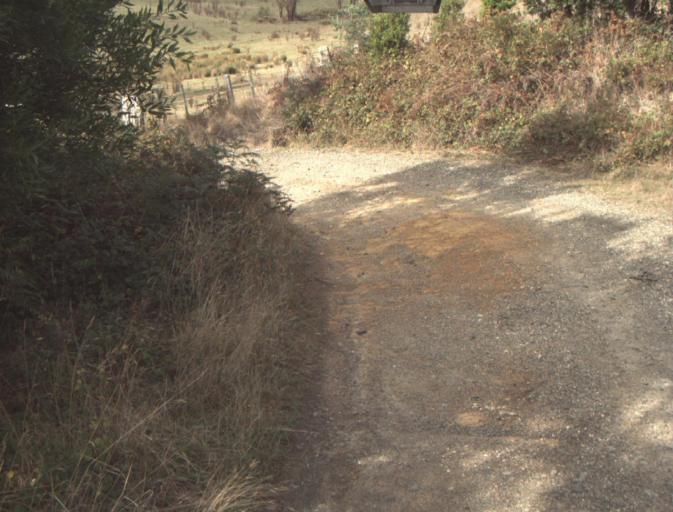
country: AU
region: Tasmania
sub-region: Launceston
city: Mayfield
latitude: -41.1808
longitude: 147.1953
